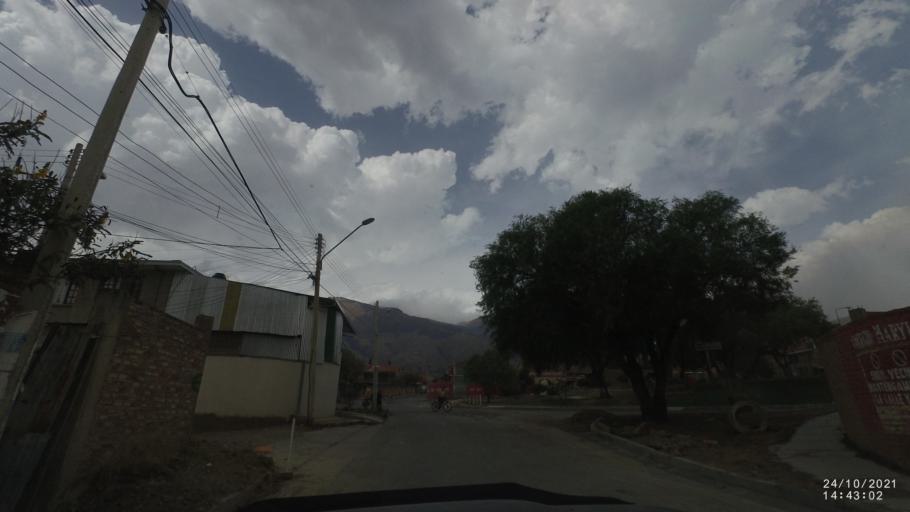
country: BO
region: Cochabamba
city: Cochabamba
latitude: -17.3491
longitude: -66.1764
